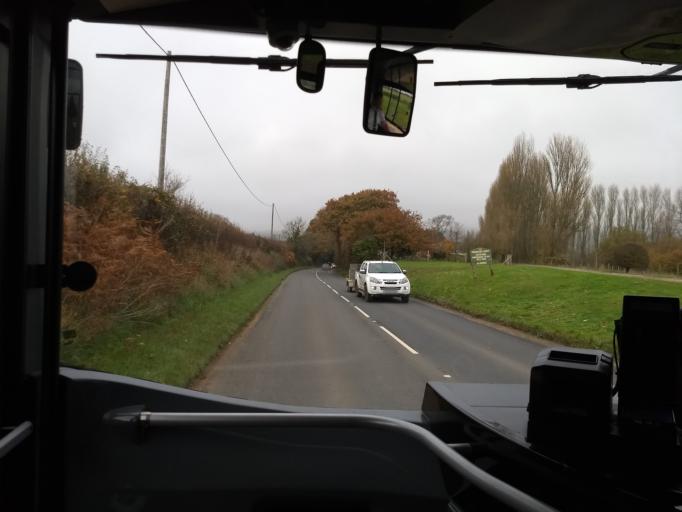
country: GB
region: England
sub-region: Isle of Wight
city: Newchurch
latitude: 50.6634
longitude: -1.2314
